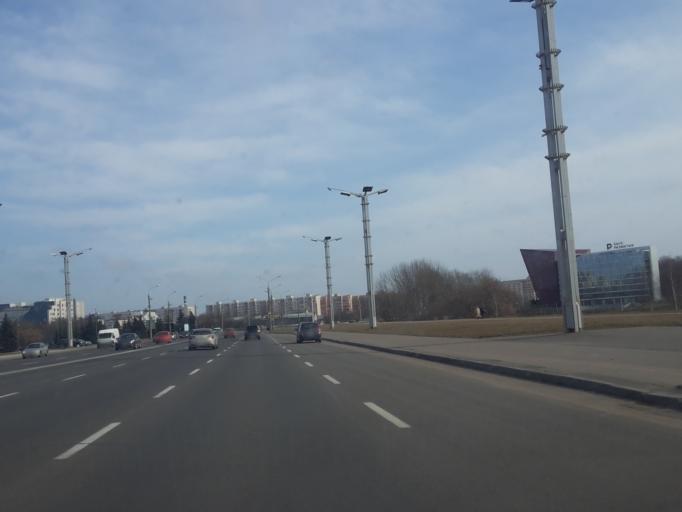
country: BY
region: Minsk
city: Minsk
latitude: 53.9155
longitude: 27.5420
